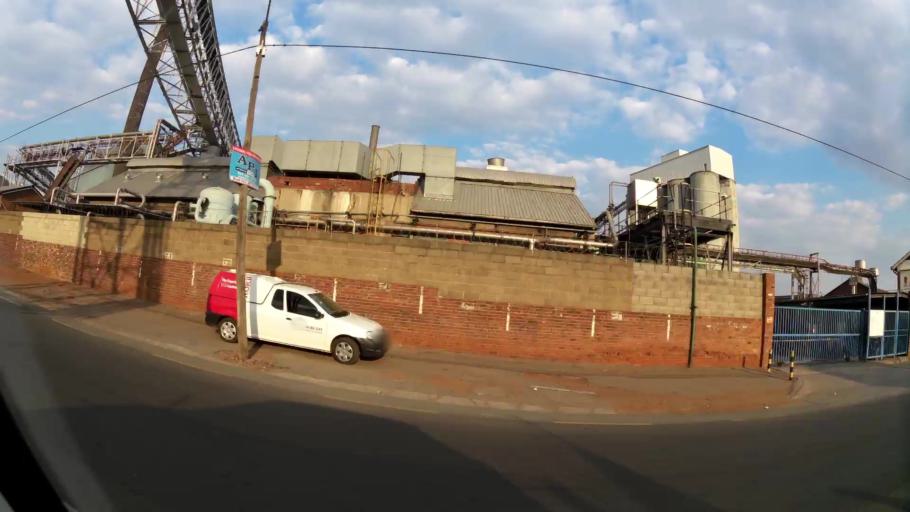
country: ZA
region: Gauteng
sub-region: Ekurhuleni Metropolitan Municipality
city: Germiston
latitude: -26.2570
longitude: 28.1856
